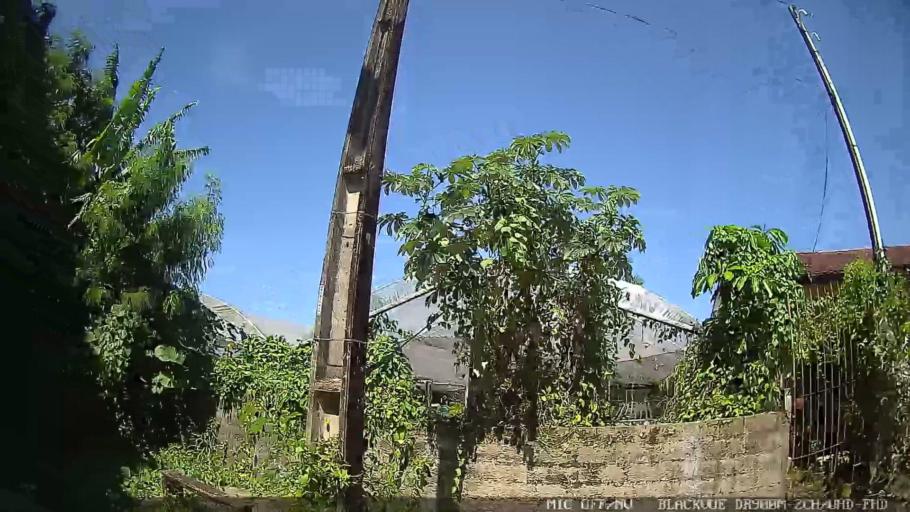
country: BR
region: Sao Paulo
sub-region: Peruibe
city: Peruibe
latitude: -24.2969
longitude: -46.9780
